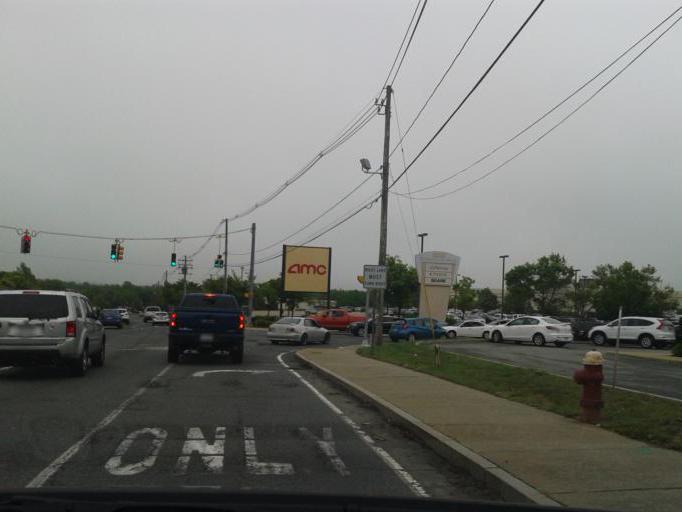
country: US
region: Massachusetts
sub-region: Bristol County
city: Smith Mills
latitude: 41.6429
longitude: -70.9885
